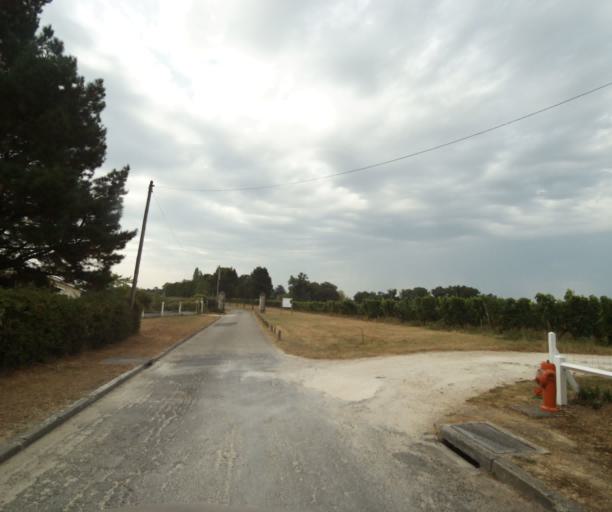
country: FR
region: Aquitaine
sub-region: Departement de la Gironde
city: Creon
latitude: 44.7674
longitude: -0.3428
